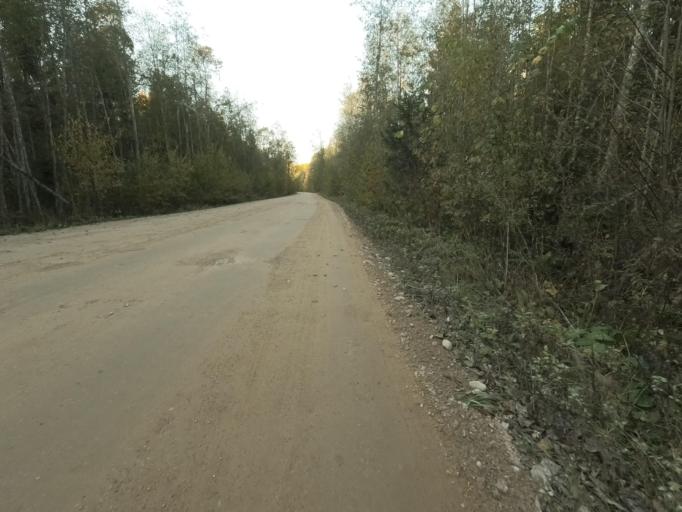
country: RU
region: Leningrad
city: Lyuban'
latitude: 58.9939
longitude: 31.1059
